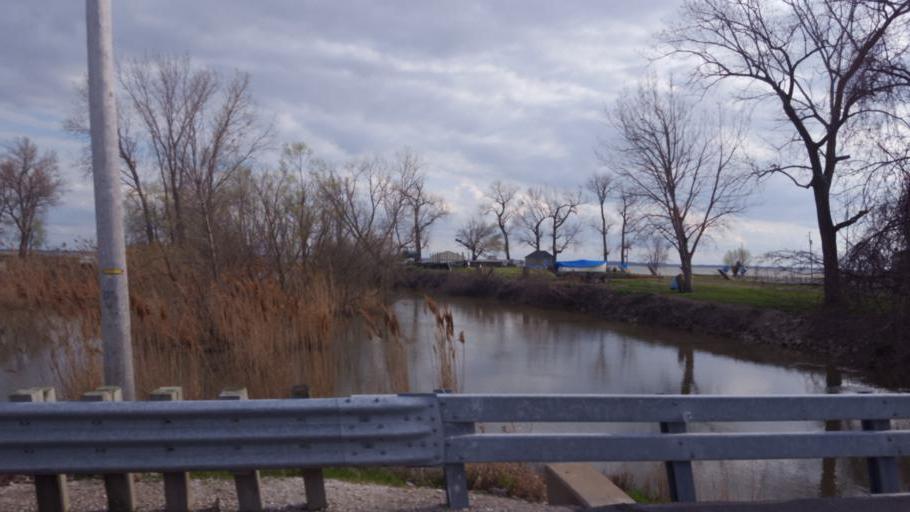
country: US
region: Ohio
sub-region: Erie County
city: Sandusky
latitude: 41.5072
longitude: -82.7754
